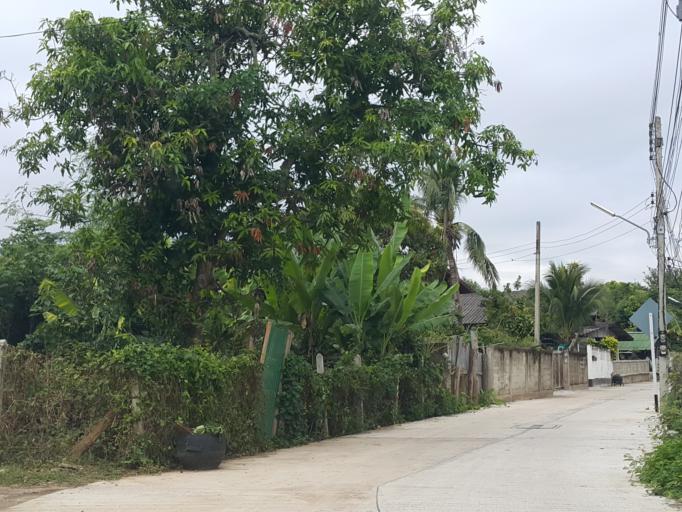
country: TH
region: Lampang
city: Lampang
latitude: 18.2968
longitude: 99.5118
